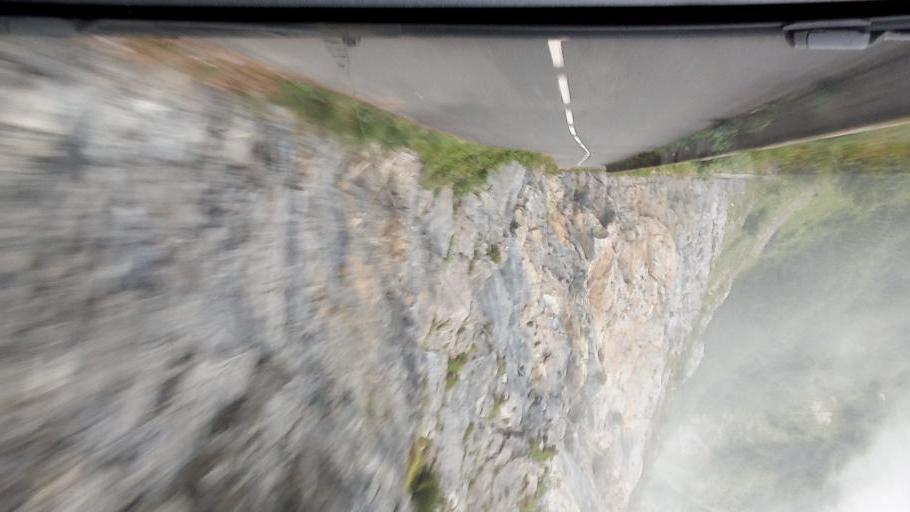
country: FR
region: Aquitaine
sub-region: Departement des Pyrenees-Atlantiques
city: Laruns
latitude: 42.9570
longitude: -0.2907
